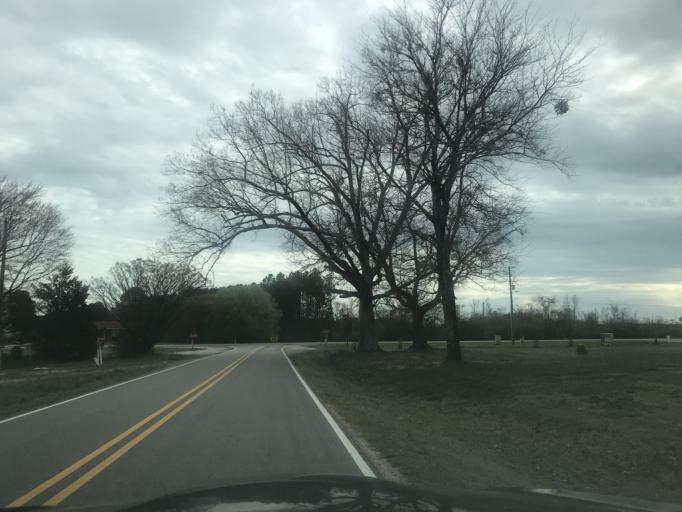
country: US
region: North Carolina
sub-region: Franklin County
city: Franklinton
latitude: 36.1150
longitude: -78.4866
